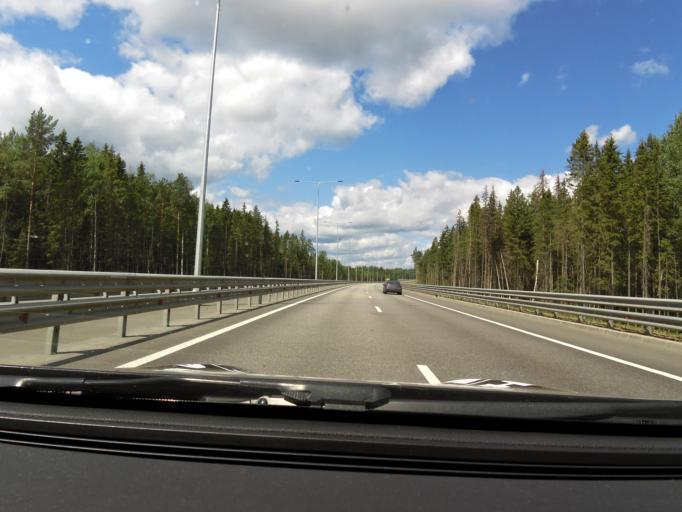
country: RU
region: Tverskaya
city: Vydropuzhsk
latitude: 57.2819
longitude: 34.8038
